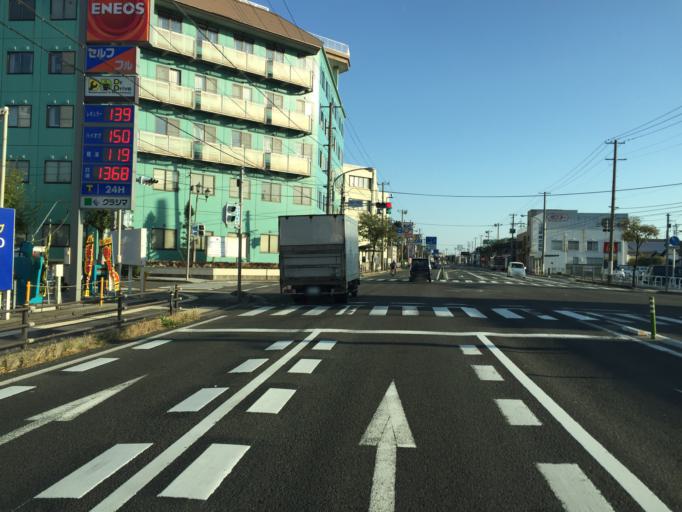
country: JP
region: Fukushima
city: Fukushima-shi
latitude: 37.7689
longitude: 140.4808
